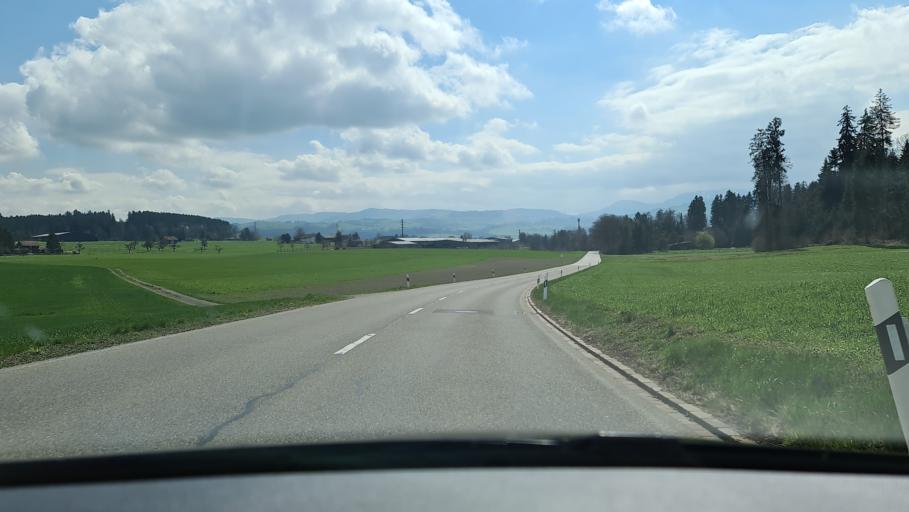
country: CH
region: Zug
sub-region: Zug
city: Steinhausen
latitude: 47.2152
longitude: 8.5045
